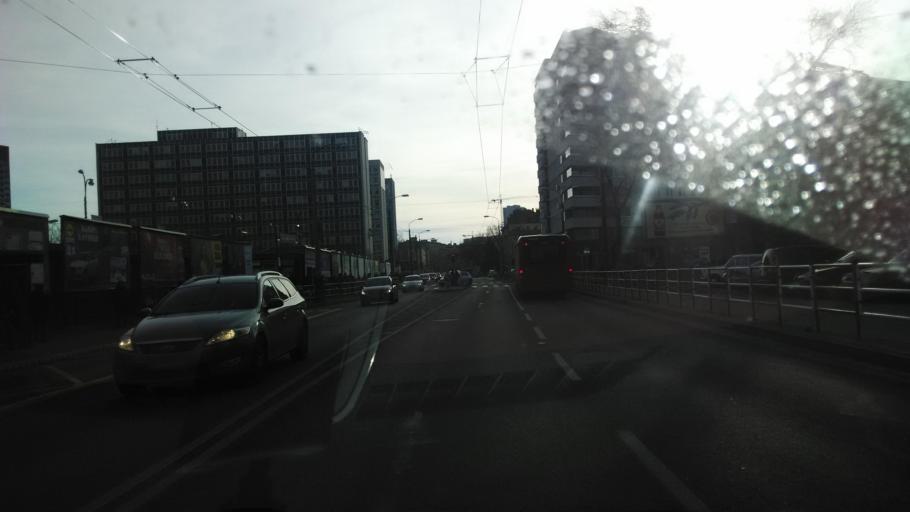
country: SK
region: Bratislavsky
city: Bratislava
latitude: 48.1537
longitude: 17.1356
